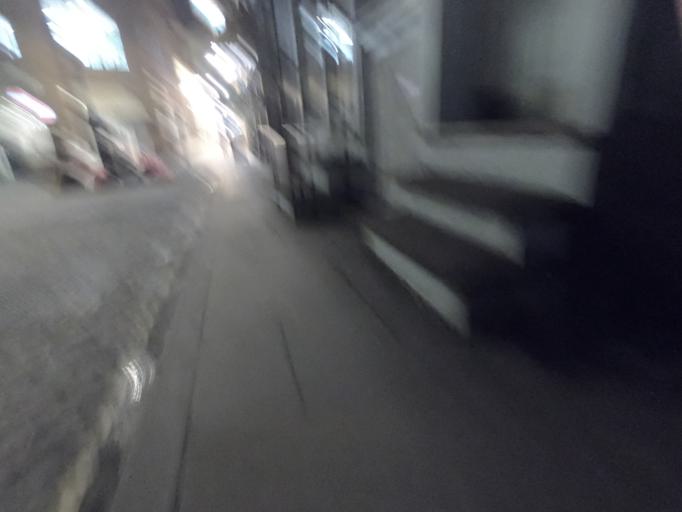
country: GB
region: England
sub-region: Greater London
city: London
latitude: 51.5125
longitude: -0.1458
